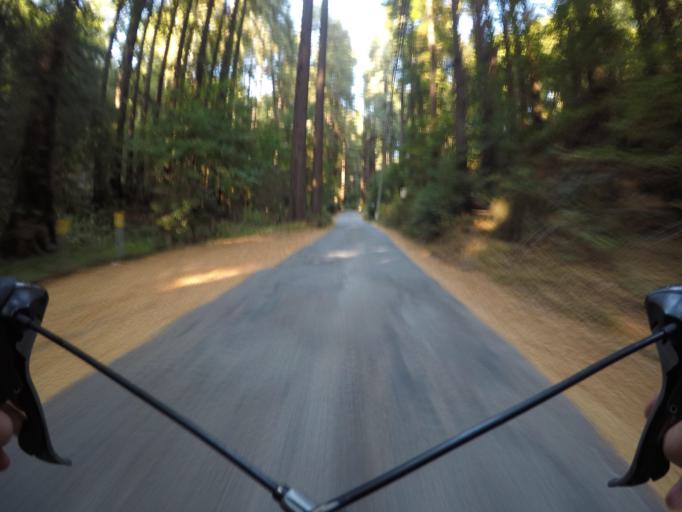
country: US
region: California
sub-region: Santa Cruz County
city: Live Oak
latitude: 37.0026
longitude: -121.9849
